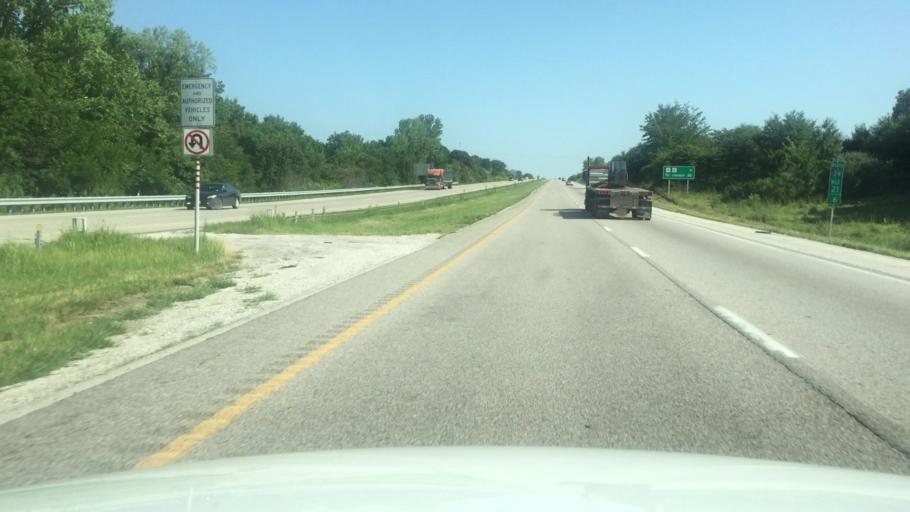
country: US
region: Missouri
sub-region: Platte County
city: Platte City
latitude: 39.3943
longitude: -94.7895
